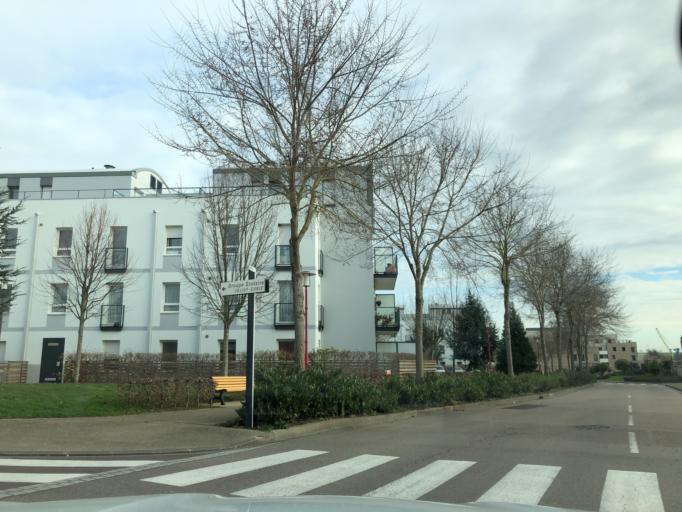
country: FR
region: Lower Normandy
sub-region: Departement du Calvados
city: Blainville-sur-Orne
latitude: 49.2293
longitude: -0.3011
